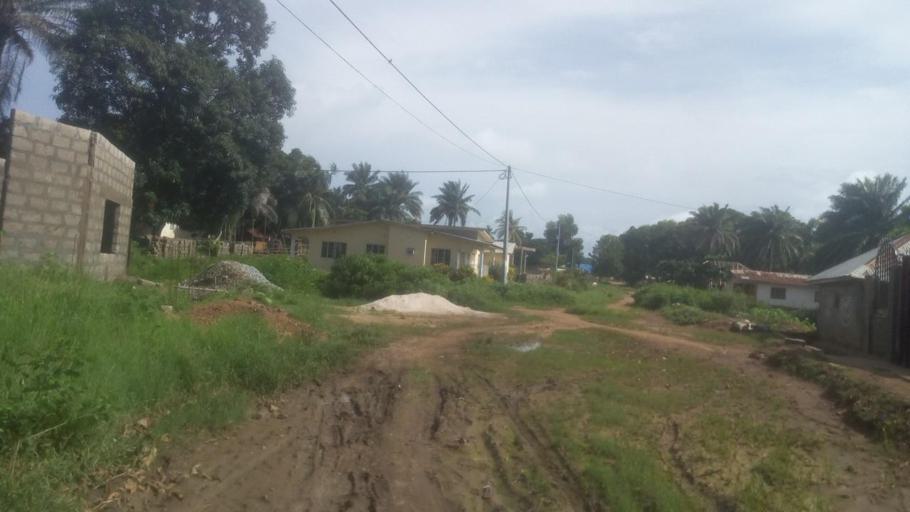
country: SL
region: Northern Province
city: Masoyila
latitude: 8.6069
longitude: -13.2001
